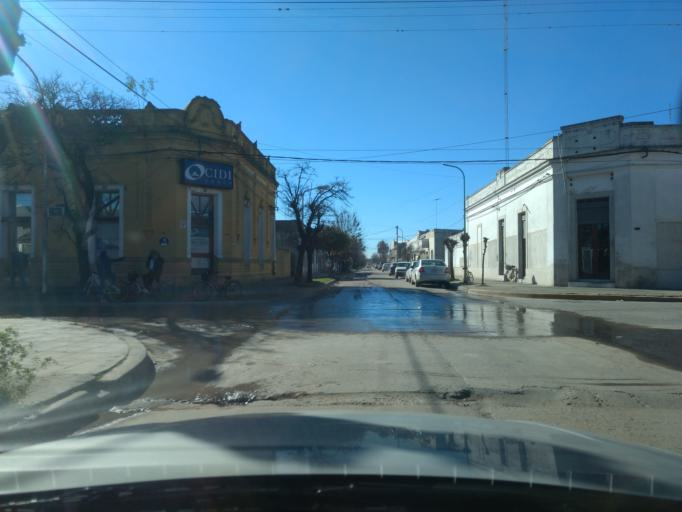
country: AR
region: Buenos Aires
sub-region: Partido de Navarro
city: Navarro
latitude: -35.0023
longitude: -59.2794
